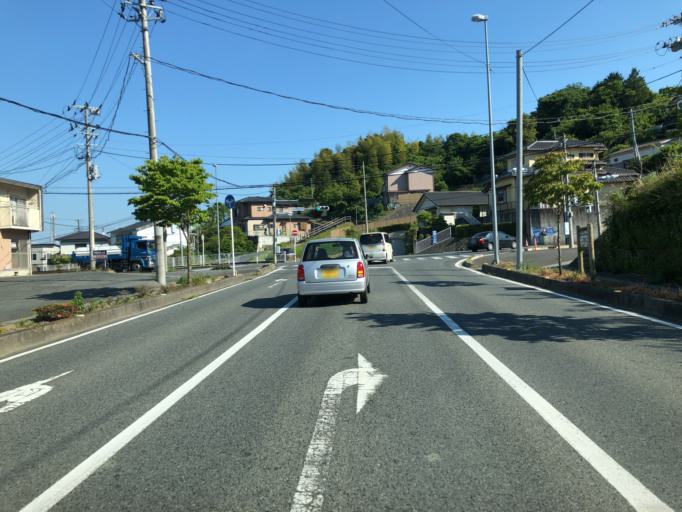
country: JP
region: Ibaraki
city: Kitaibaraki
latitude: 36.9252
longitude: 140.7927
